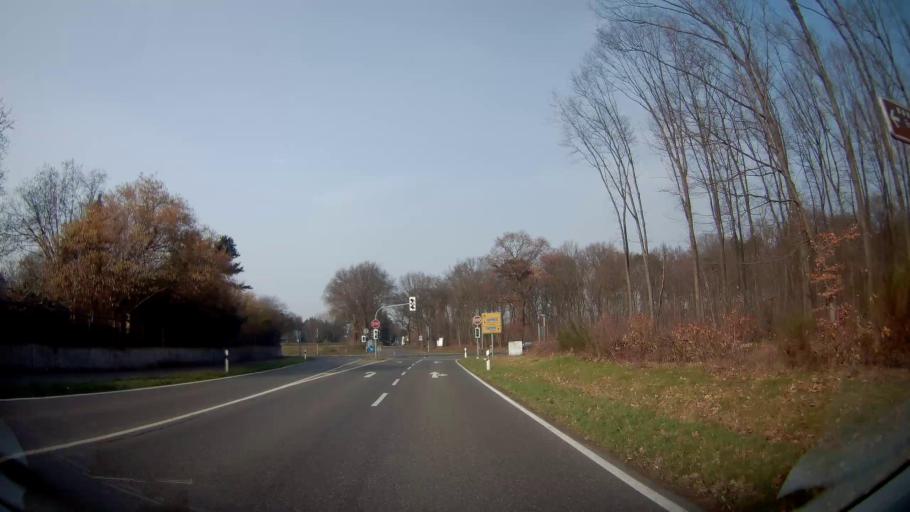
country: DE
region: North Rhine-Westphalia
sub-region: Regierungsbezirk Dusseldorf
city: Moers
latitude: 51.4891
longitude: 6.6381
